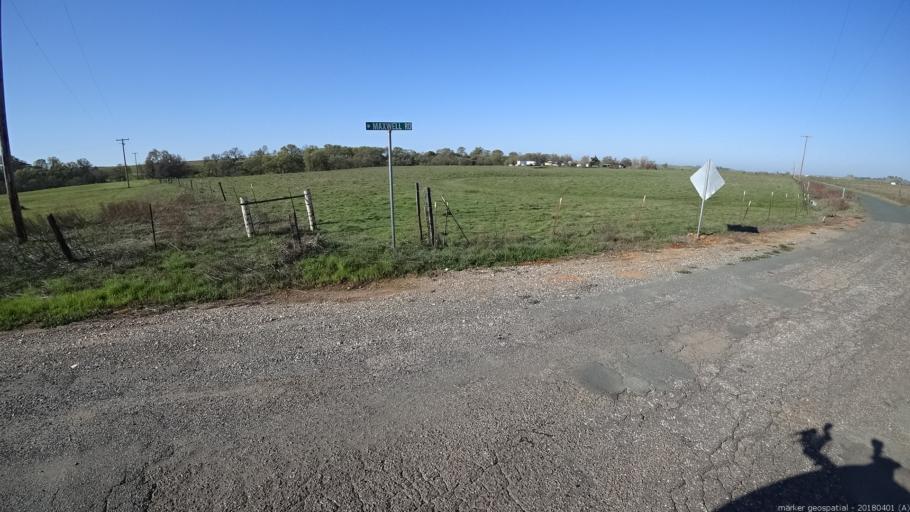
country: US
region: California
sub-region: Sacramento County
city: Rancho Murieta
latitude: 38.4201
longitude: -121.0248
